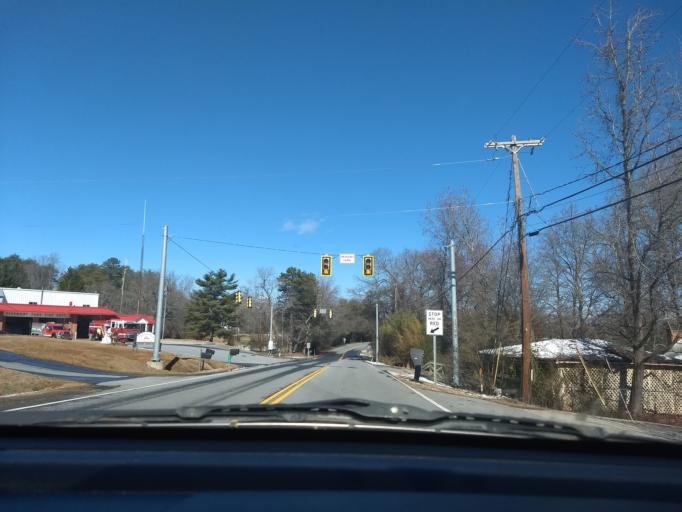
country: US
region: South Carolina
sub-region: Greenville County
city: Wade Hampton
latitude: 34.9120
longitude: -82.3724
